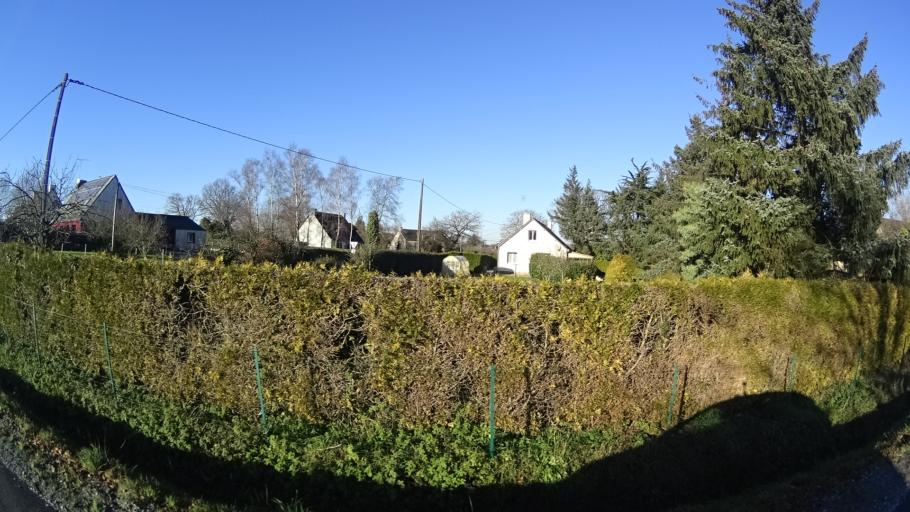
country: FR
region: Brittany
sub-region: Departement du Morbihan
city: Allaire
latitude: 47.6388
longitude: -2.1714
